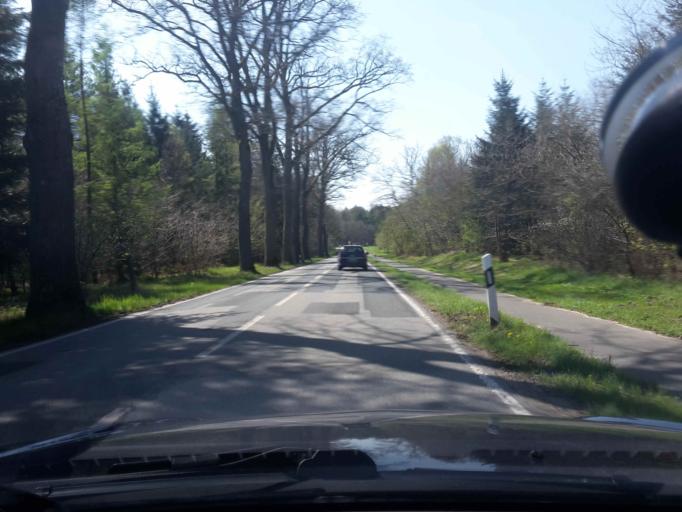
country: DE
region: Lower Saxony
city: Handeloh
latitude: 53.2714
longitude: 9.8787
